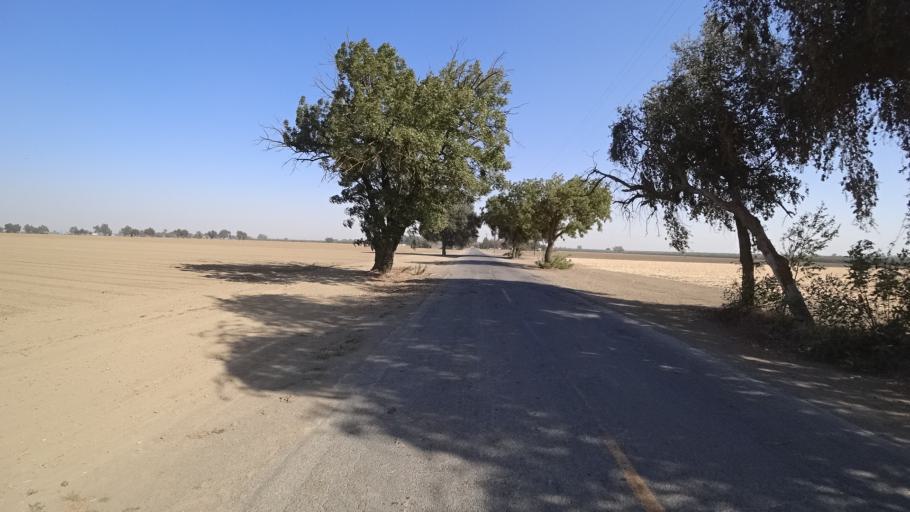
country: US
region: California
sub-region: Yolo County
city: Woodland
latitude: 38.7356
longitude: -121.8362
